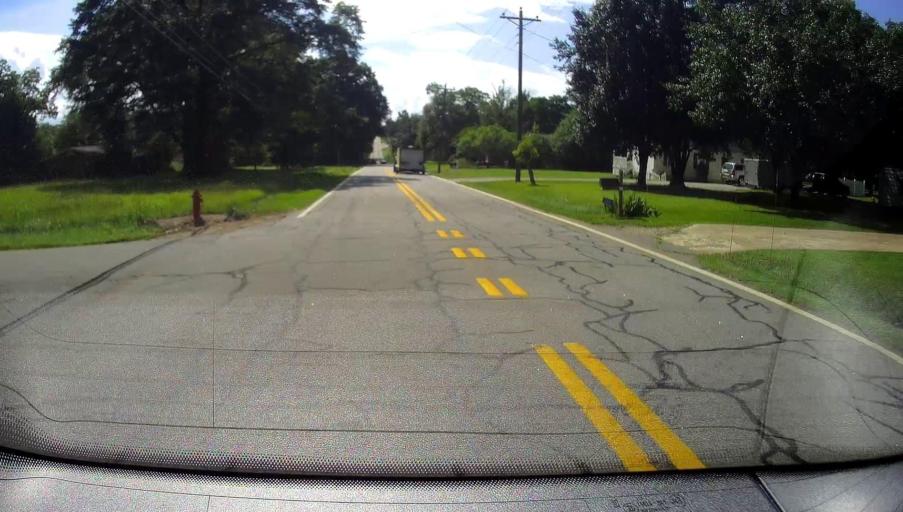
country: US
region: Georgia
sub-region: Upson County
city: Hannahs Mill
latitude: 32.9349
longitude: -84.3424
